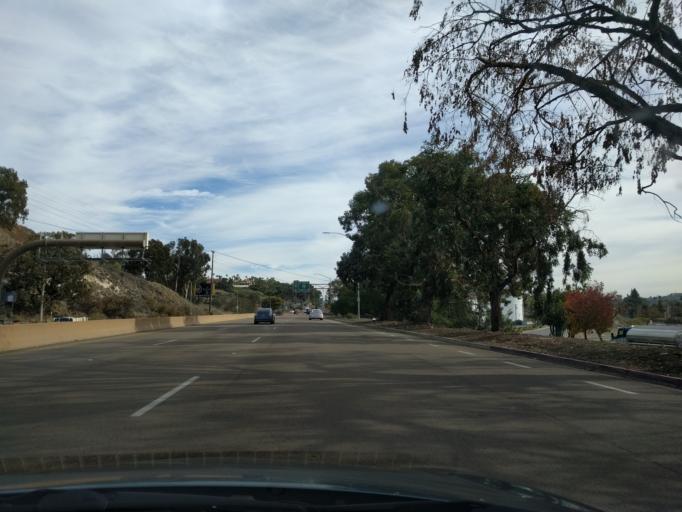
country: US
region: California
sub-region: San Diego County
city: San Diego
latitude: 32.7870
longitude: -117.1189
